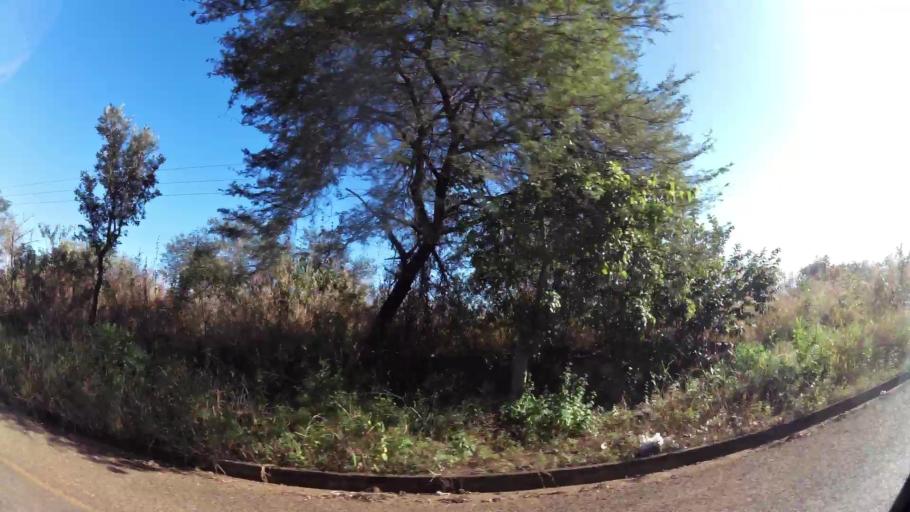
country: ZA
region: Limpopo
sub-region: Mopani District Municipality
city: Tzaneen
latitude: -23.8423
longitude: 30.1286
